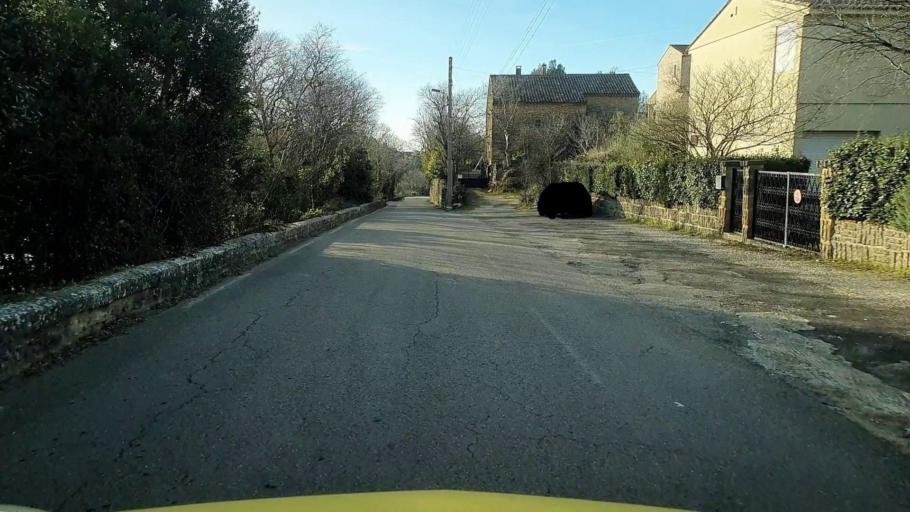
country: FR
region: Languedoc-Roussillon
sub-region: Departement du Gard
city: Castillon-du-Gard
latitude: 43.9680
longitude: 4.5547
